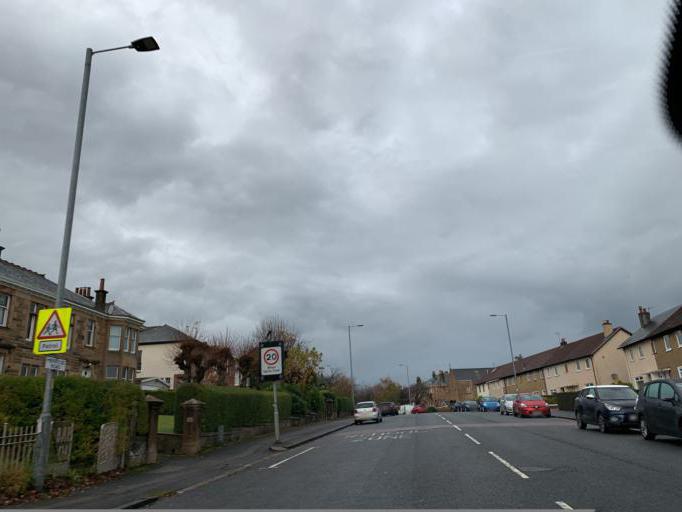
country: GB
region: Scotland
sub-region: East Renfrewshire
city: Giffnock
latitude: 55.8144
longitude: -4.2728
